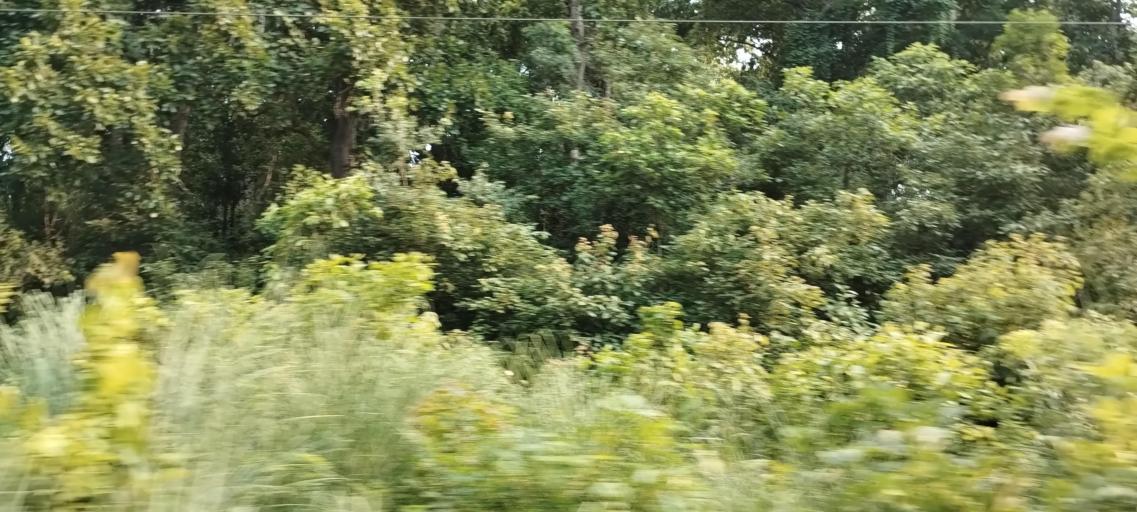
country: NP
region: Mid Western
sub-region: Bheri Zone
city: Bardiya
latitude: 28.4311
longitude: 81.3629
